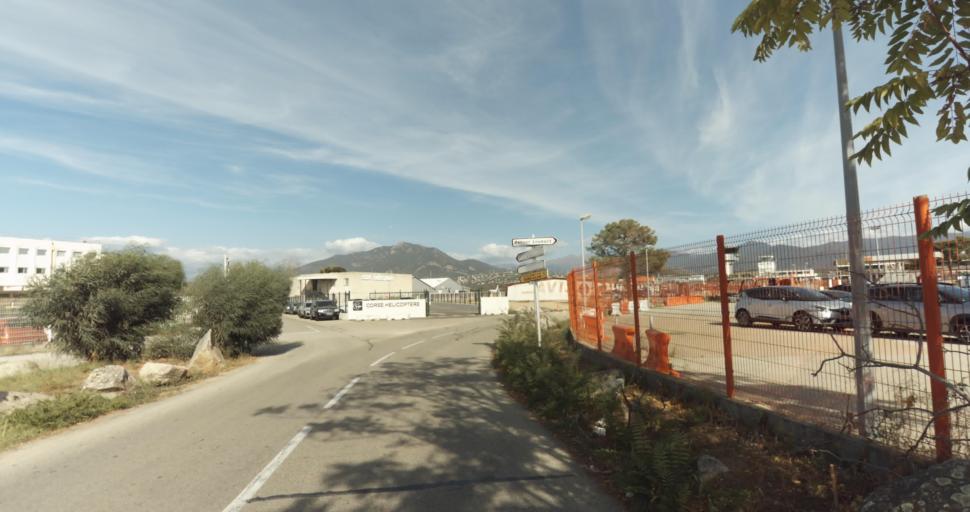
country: FR
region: Corsica
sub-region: Departement de la Corse-du-Sud
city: Ajaccio
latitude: 41.9214
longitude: 8.7908
